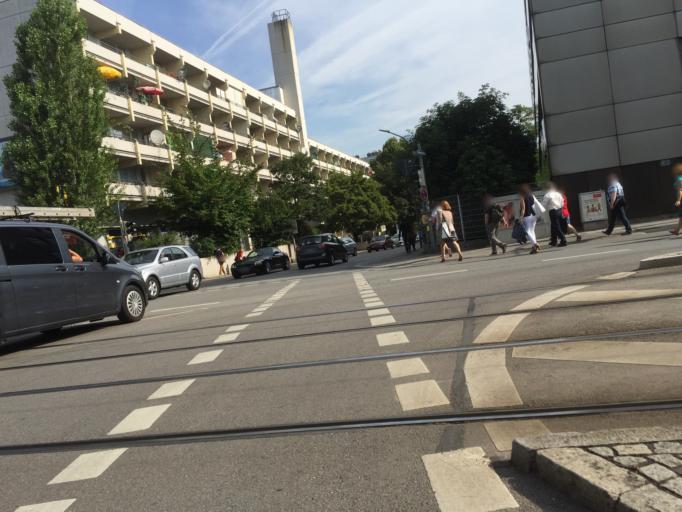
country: DE
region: Bavaria
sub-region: Upper Bavaria
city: Bogenhausen
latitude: 48.1297
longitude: 11.6230
